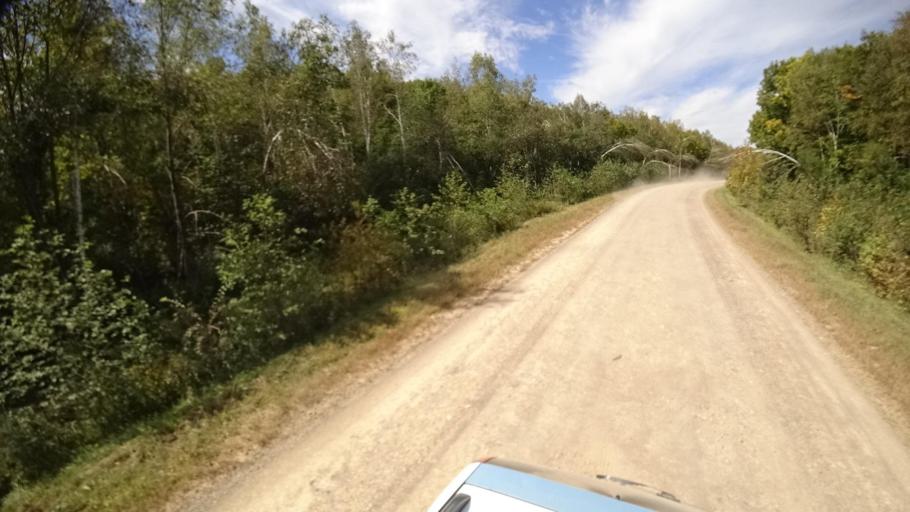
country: RU
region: Primorskiy
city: Yakovlevka
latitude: 44.6600
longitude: 133.7284
